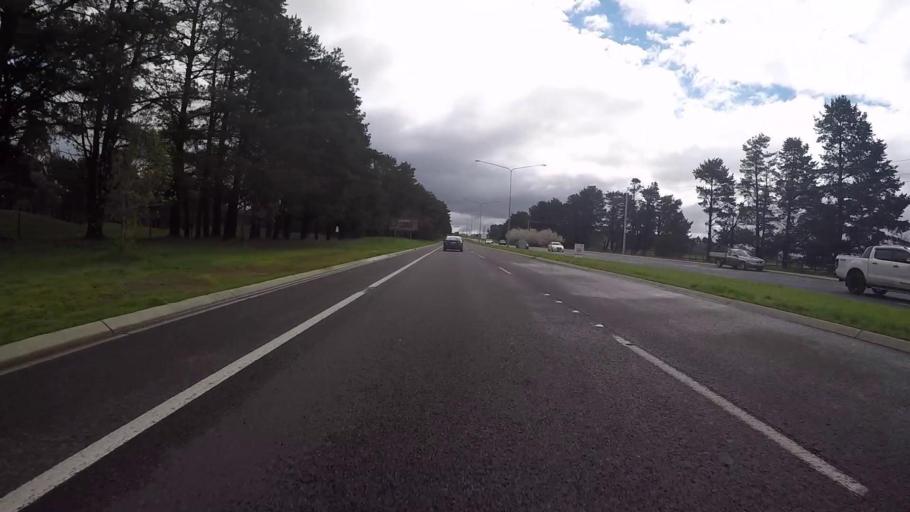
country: AU
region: Australian Capital Territory
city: Kaleen
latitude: -35.2376
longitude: 149.1336
